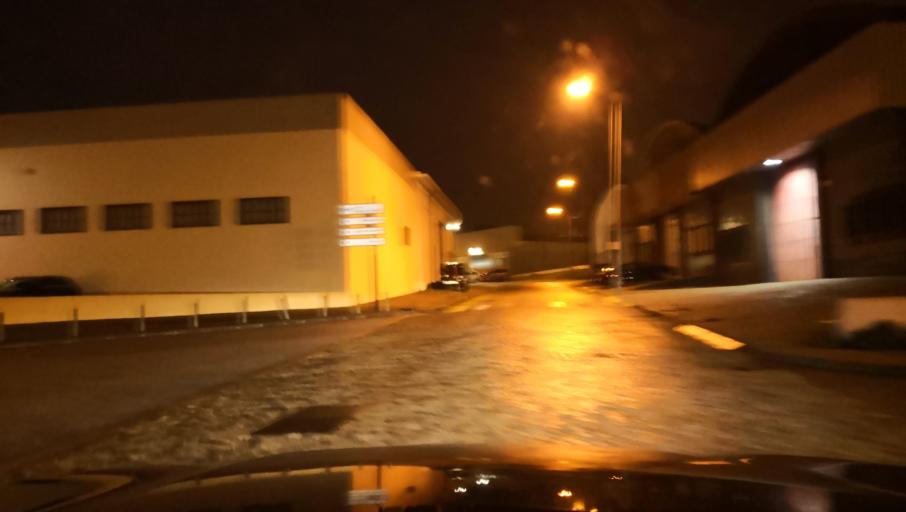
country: PT
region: Porto
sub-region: Matosinhos
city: Guifoes
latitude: 41.2033
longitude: -8.6850
